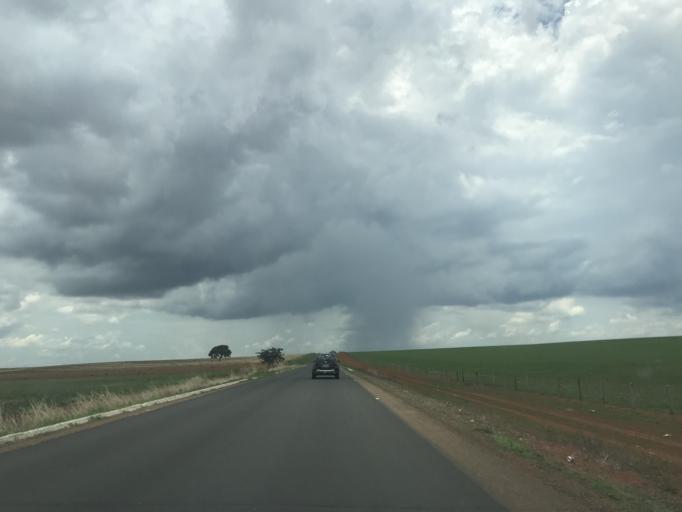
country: BR
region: Goias
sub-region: Vianopolis
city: Vianopolis
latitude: -16.8184
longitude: -48.5247
